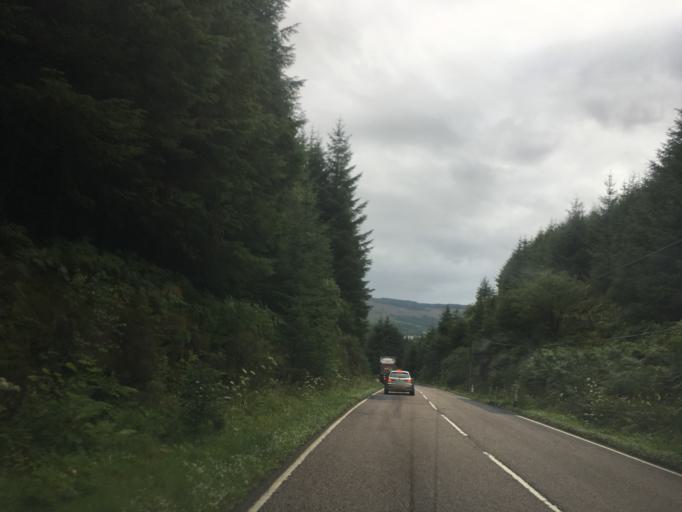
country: GB
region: Scotland
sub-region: Argyll and Bute
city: Oban
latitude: 56.2811
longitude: -5.4831
